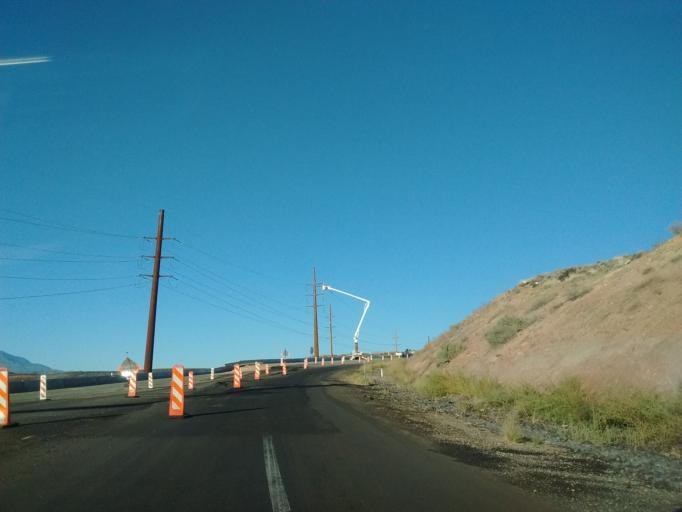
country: US
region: Utah
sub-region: Washington County
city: Washington
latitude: 37.1350
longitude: -113.4779
